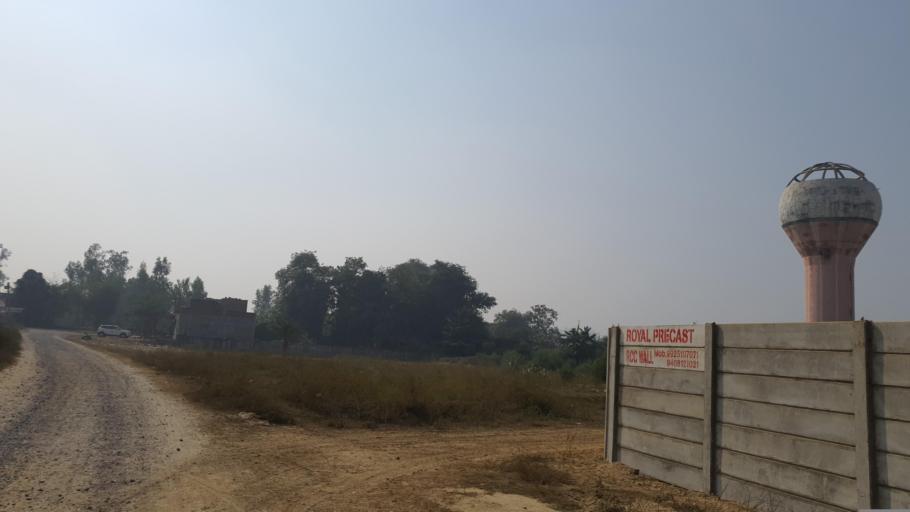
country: IN
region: Uttar Pradesh
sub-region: Lucknow District
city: Goshainganj
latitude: 26.7743
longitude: 81.0131
